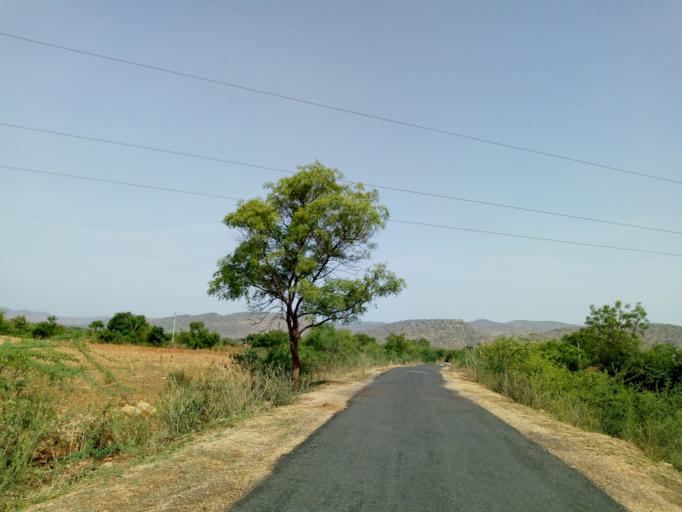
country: IN
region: Andhra Pradesh
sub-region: Prakasam
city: Cumbum
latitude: 15.7134
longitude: 79.0834
